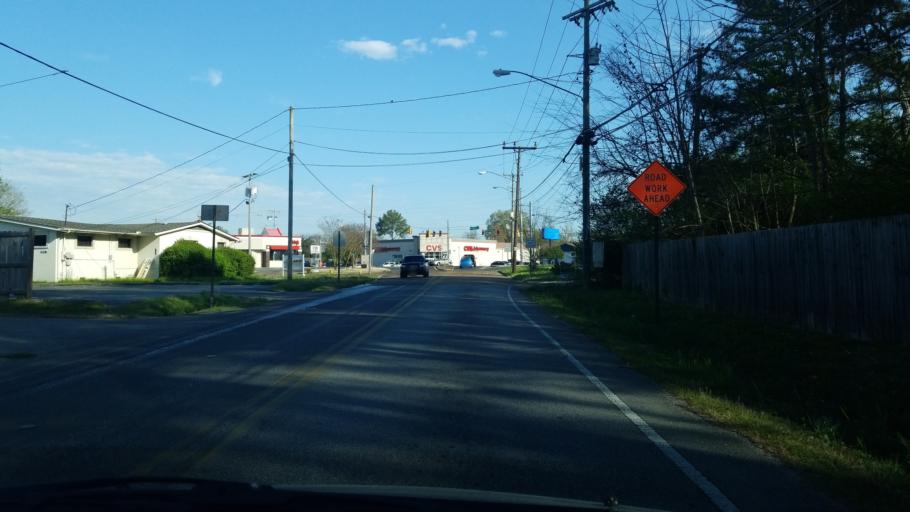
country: US
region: Tennessee
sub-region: Hamilton County
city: East Ridge
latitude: 35.0087
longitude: -85.2199
